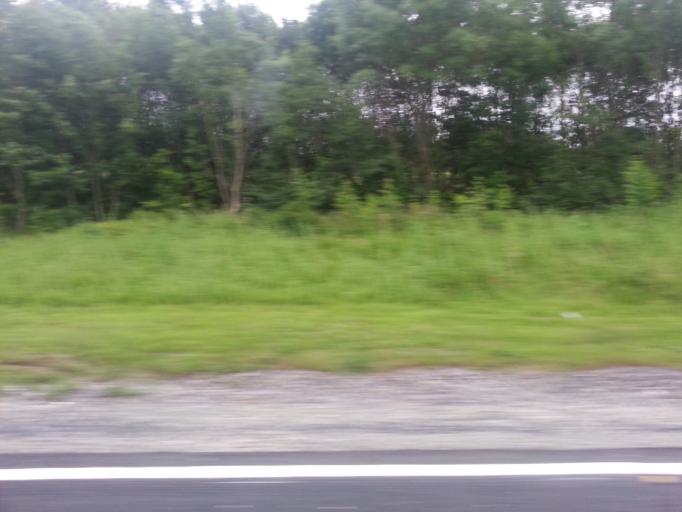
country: IE
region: Leinster
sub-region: Kildare
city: Kilcullen
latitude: 53.1661
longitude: -6.7576
